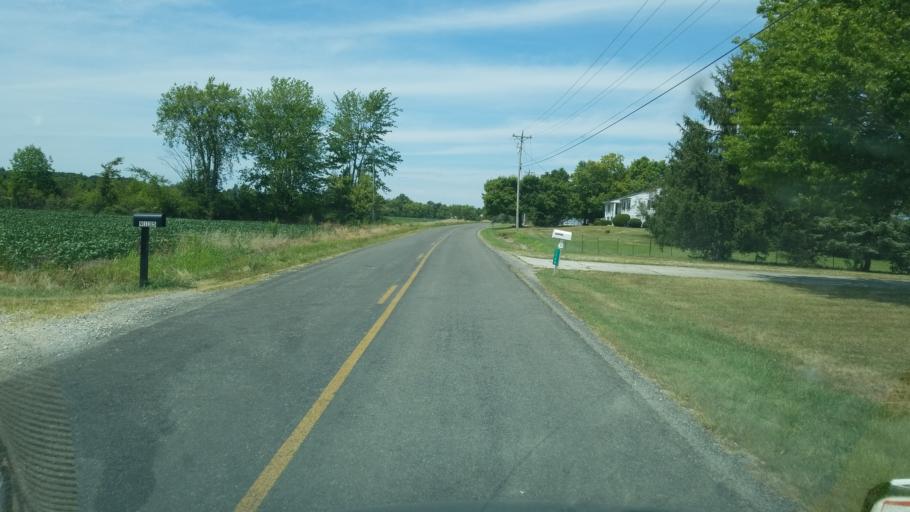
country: US
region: Ohio
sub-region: Union County
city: New California
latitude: 40.1412
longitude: -83.2552
